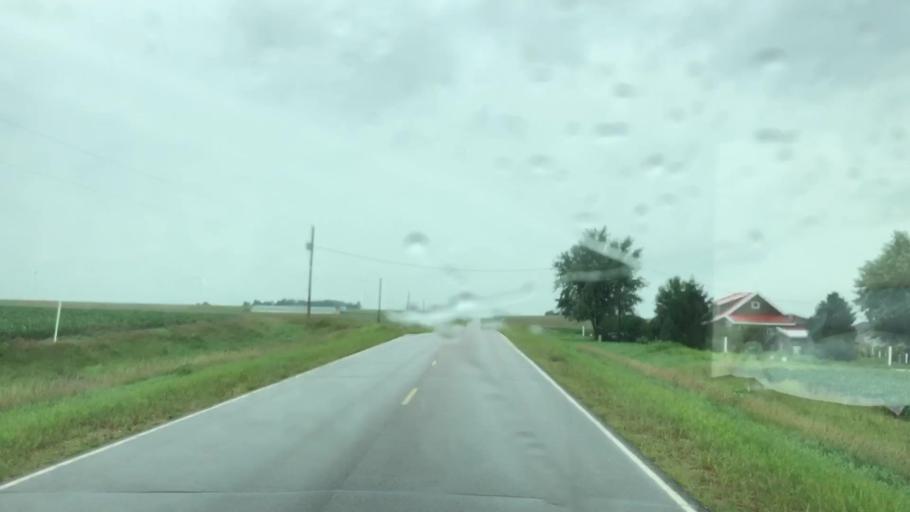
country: US
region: Iowa
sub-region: O'Brien County
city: Sanborn
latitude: 43.2122
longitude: -95.7233
